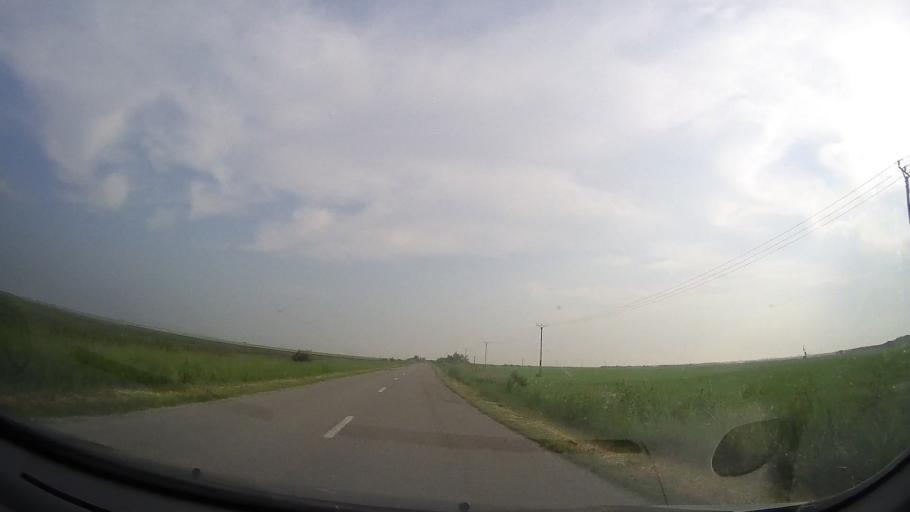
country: RO
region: Timis
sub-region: Comuna Giulvaz
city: Giulvaz
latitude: 45.5366
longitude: 20.9483
